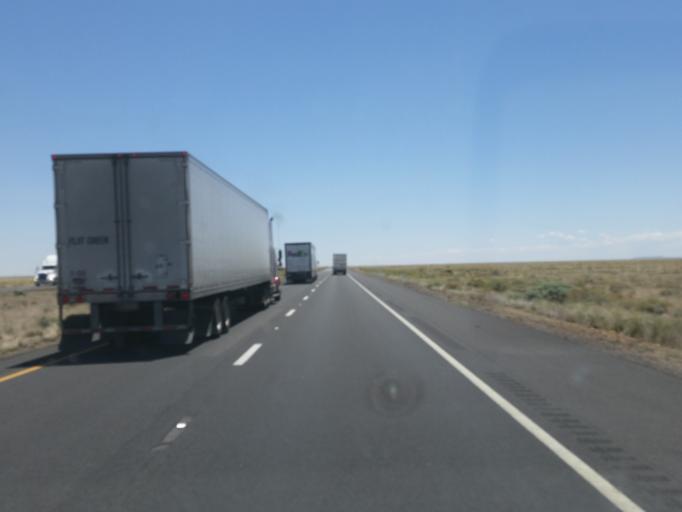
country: US
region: Arizona
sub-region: Coconino County
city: Flagstaff
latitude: 35.1496
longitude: -111.2402
